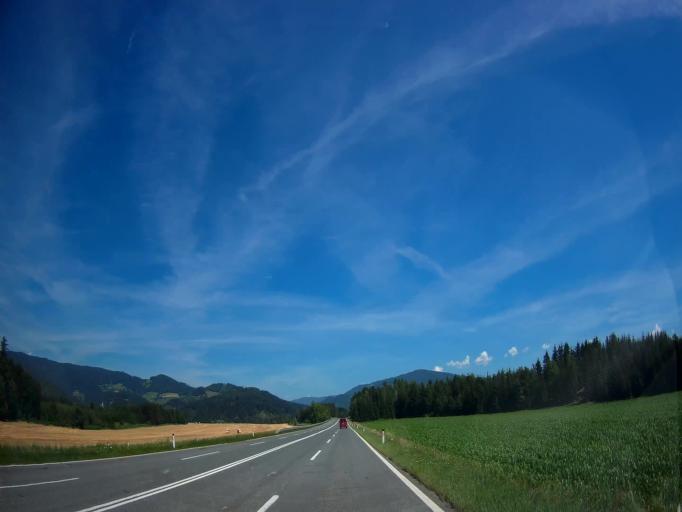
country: AT
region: Carinthia
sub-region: Politischer Bezirk Sankt Veit an der Glan
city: Molbling
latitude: 46.8489
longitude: 14.4482
